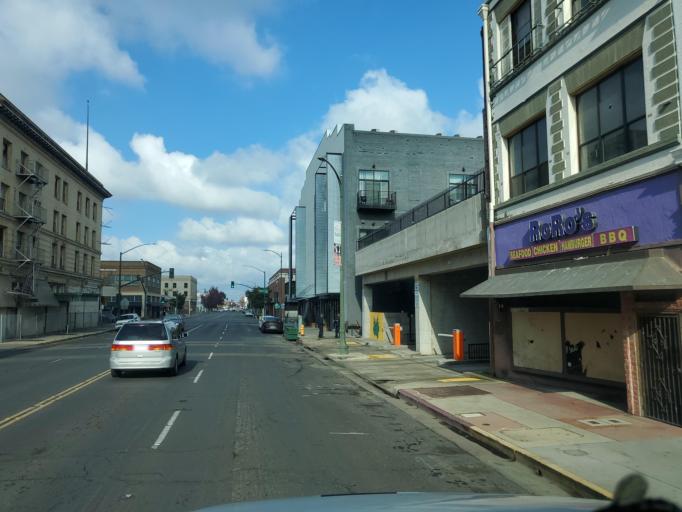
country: US
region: California
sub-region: San Joaquin County
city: Stockton
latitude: 37.9539
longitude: -121.2846
